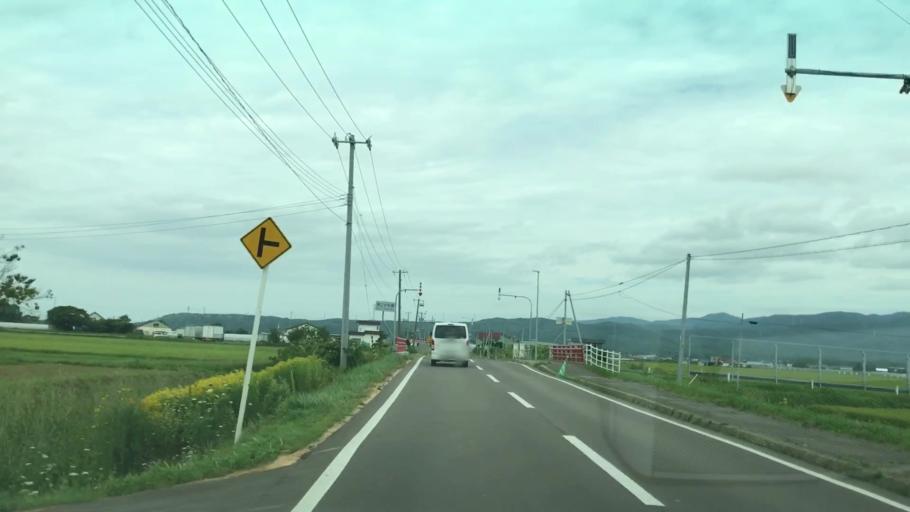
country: JP
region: Hokkaido
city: Iwanai
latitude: 43.0093
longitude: 140.5778
